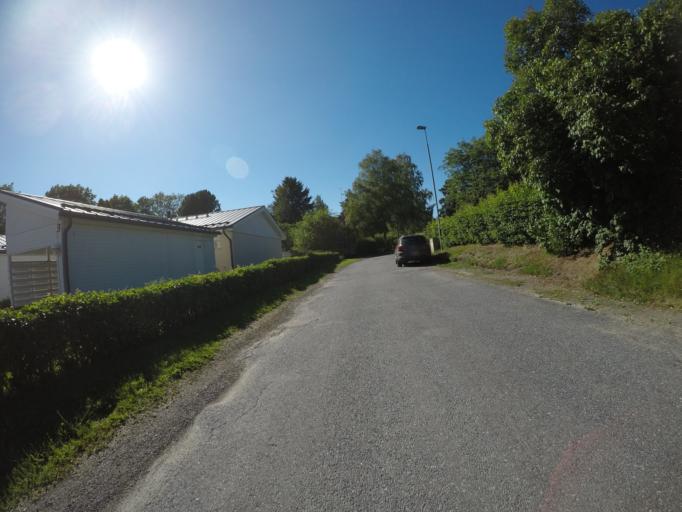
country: FI
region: Haeme
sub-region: Haemeenlinna
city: Haemeenlinna
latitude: 61.0065
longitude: 24.4828
